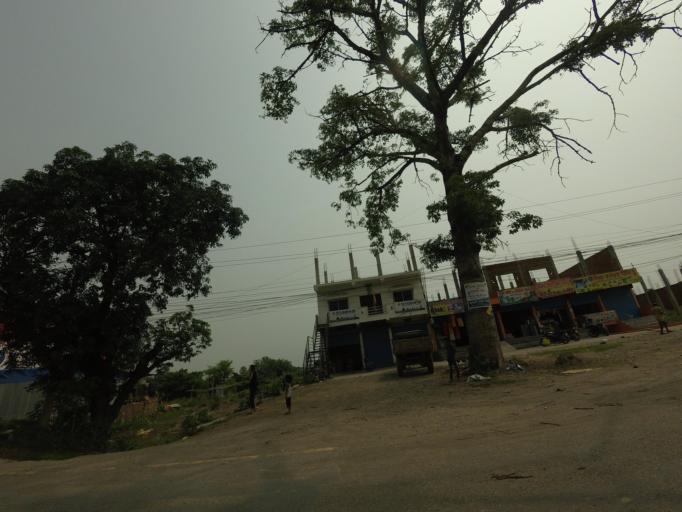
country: NP
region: Western Region
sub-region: Lumbini Zone
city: Bhairahawa
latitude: 27.5139
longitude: 83.3978
